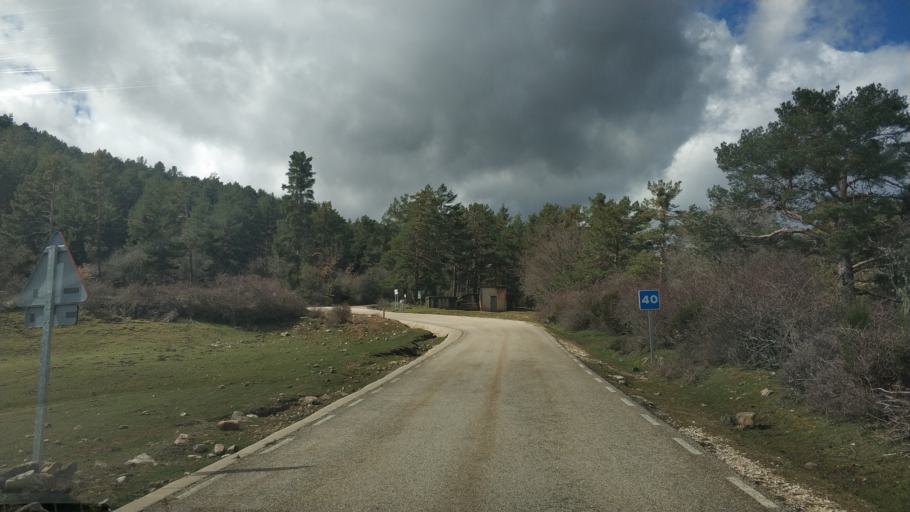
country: ES
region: Castille and Leon
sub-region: Provincia de Burgos
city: Neila
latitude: 42.0570
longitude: -3.0110
